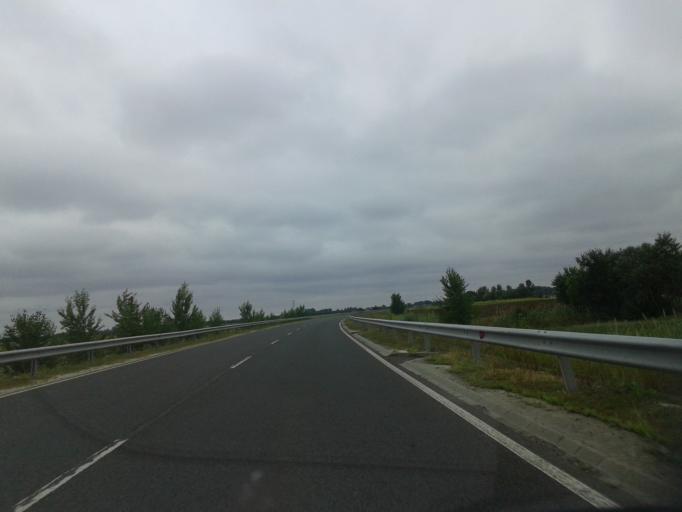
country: HU
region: Bacs-Kiskun
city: Harta
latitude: 46.7192
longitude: 19.0217
